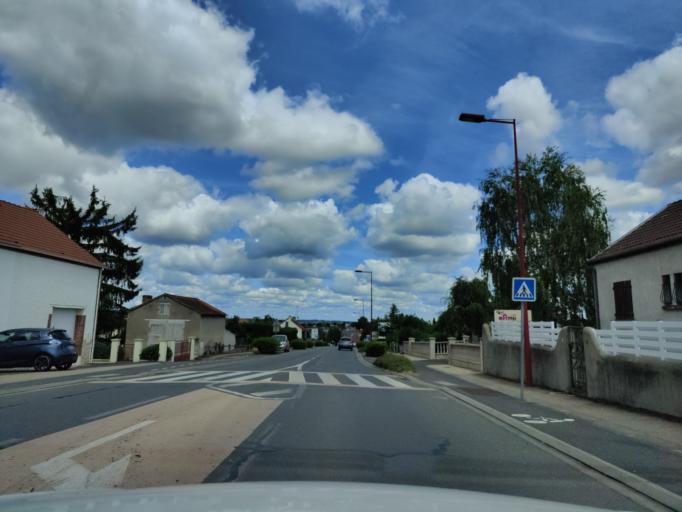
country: FR
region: Auvergne
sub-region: Departement de l'Allier
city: Saint-Victor
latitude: 46.3768
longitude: 2.6194
